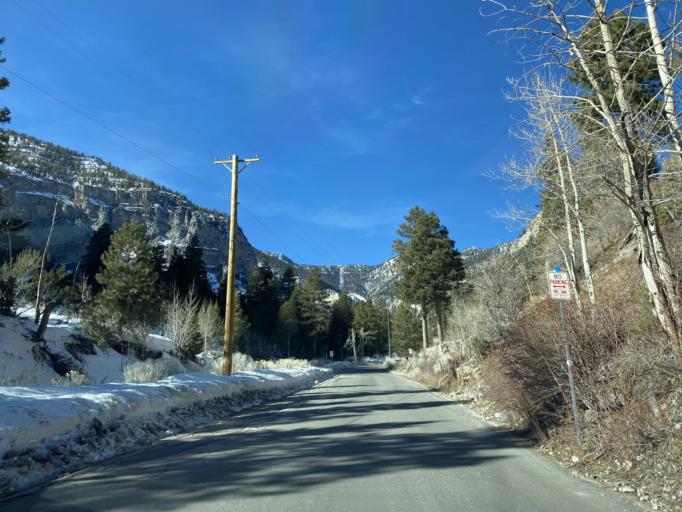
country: US
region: Nevada
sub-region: Nye County
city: Pahrump
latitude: 36.2643
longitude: -115.6571
